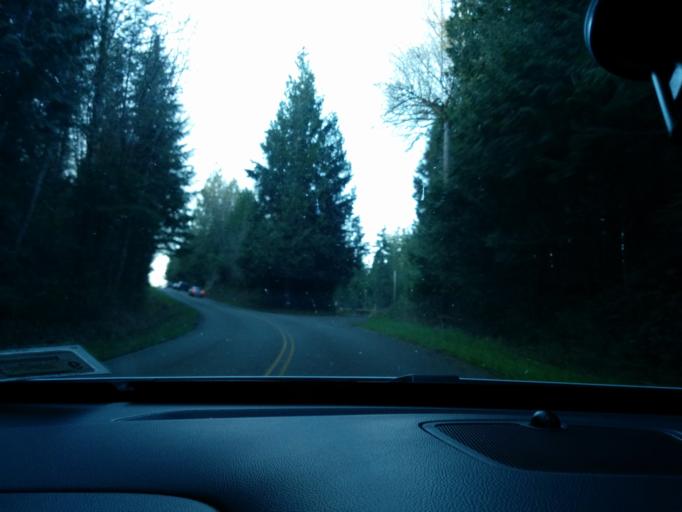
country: US
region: Washington
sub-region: Snohomish County
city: Gold Bar
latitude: 47.8878
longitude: -121.7348
